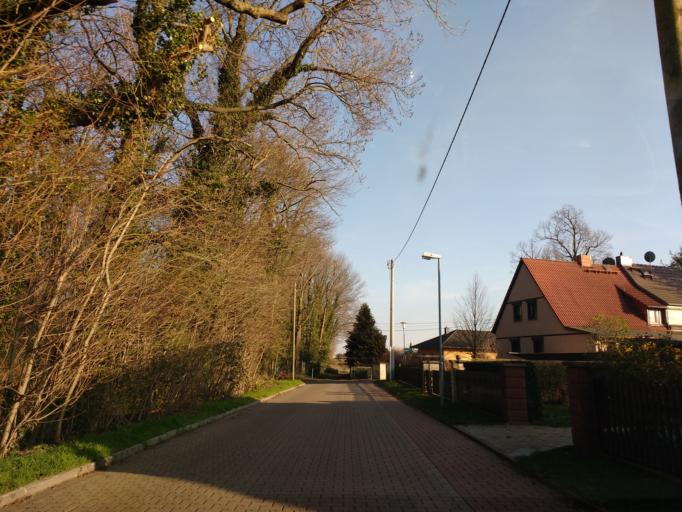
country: DE
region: Saxony-Anhalt
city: Oppin
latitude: 51.5499
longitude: 12.0307
